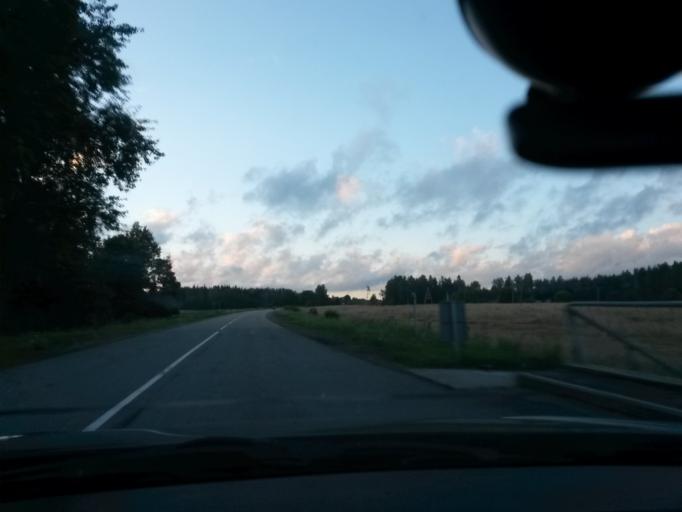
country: LV
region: Jekabpils Rajons
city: Jekabpils
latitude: 56.7004
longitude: 25.9811
